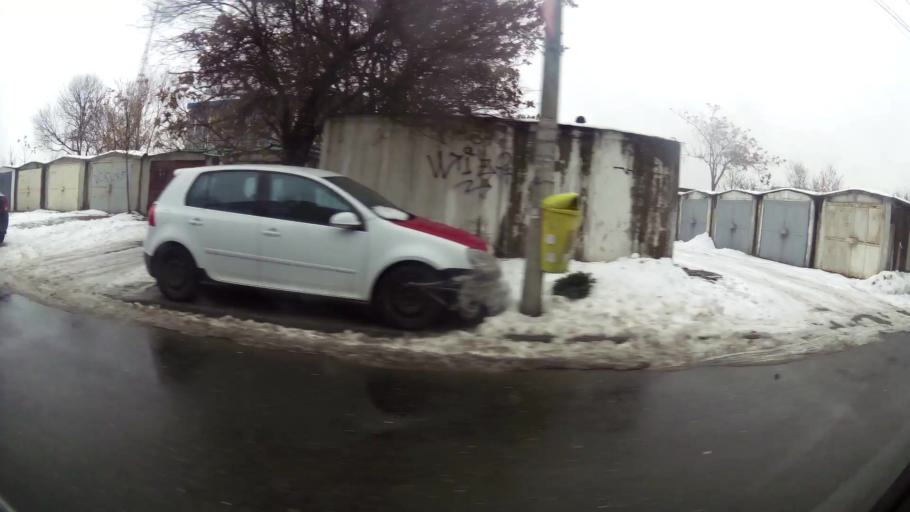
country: RO
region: Ilfov
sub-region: Comuna Chiajna
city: Rosu
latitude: 44.4382
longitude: 26.0402
